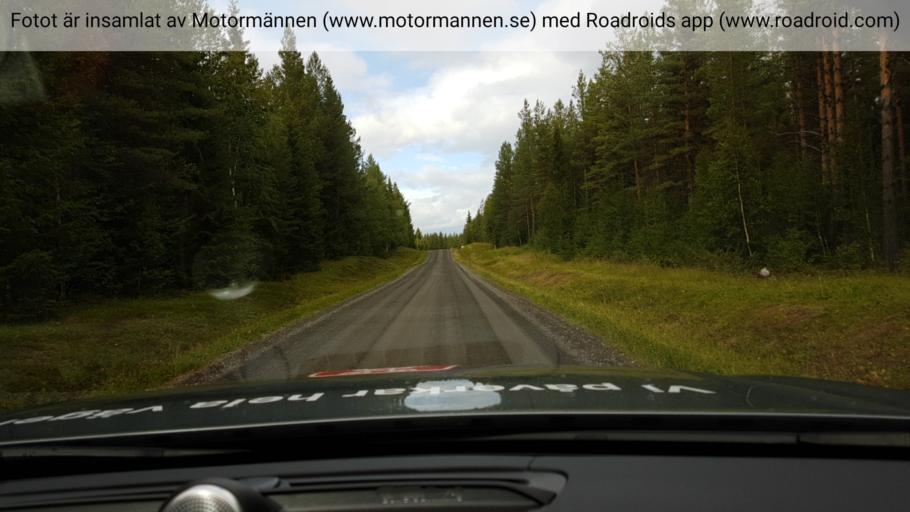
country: SE
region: Jaemtland
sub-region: OEstersunds Kommun
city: Lit
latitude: 63.7601
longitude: 14.6606
